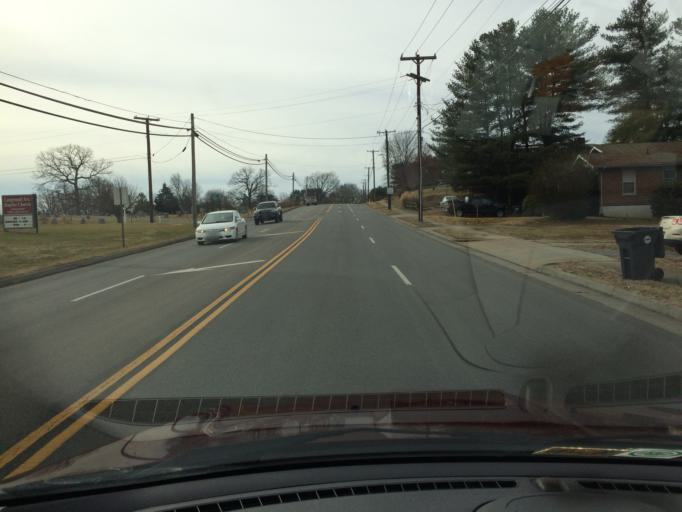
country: US
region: Virginia
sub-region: City of Bedford
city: Bedford
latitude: 37.3449
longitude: -79.5093
